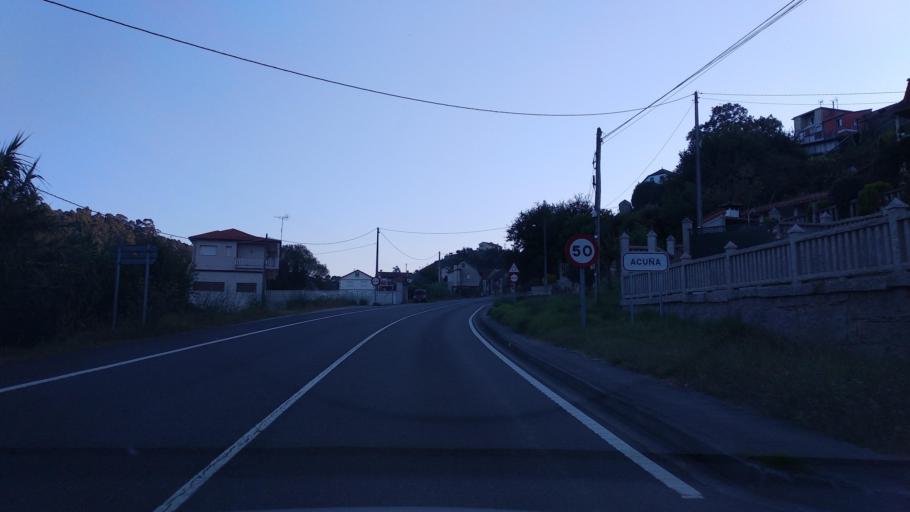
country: ES
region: Galicia
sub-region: Provincia de Pontevedra
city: Marin
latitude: 42.3493
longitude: -8.6422
